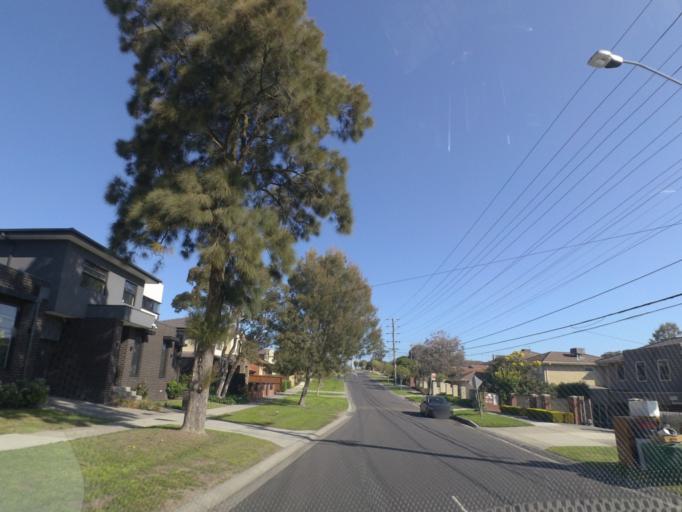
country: AU
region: Victoria
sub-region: Boroondara
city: Balwyn North
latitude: -37.7811
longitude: 145.1034
